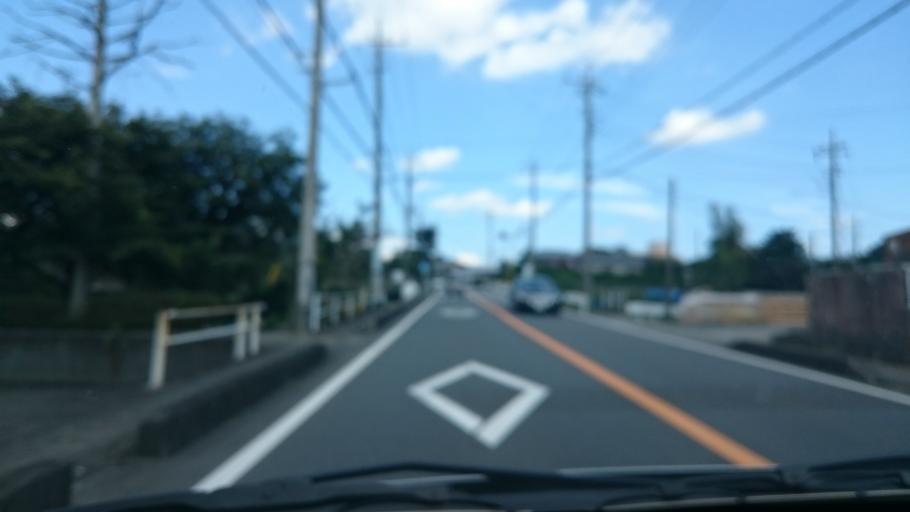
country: JP
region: Shizuoka
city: Gotemba
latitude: 35.2299
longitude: 138.9207
